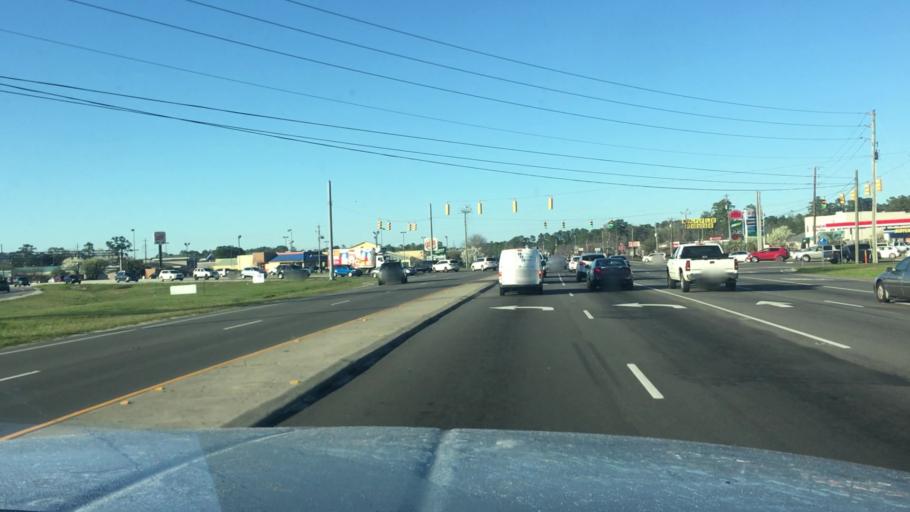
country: US
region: North Carolina
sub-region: New Hanover County
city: Myrtle Grove
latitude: 34.1391
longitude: -77.8939
